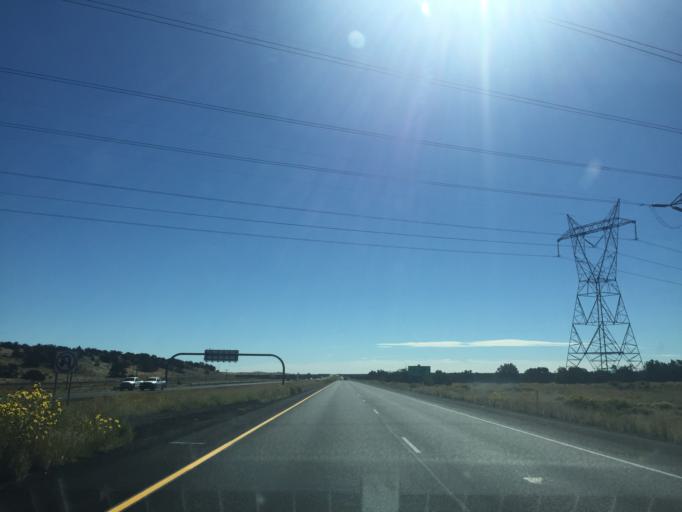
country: US
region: Arizona
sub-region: Coconino County
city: Flagstaff
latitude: 35.1964
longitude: -111.3942
